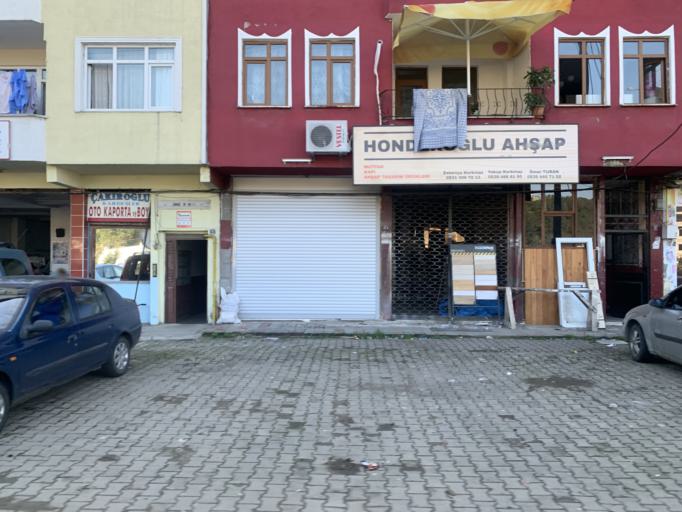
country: TR
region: Trabzon
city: Of
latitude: 40.9397
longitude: 40.2707
